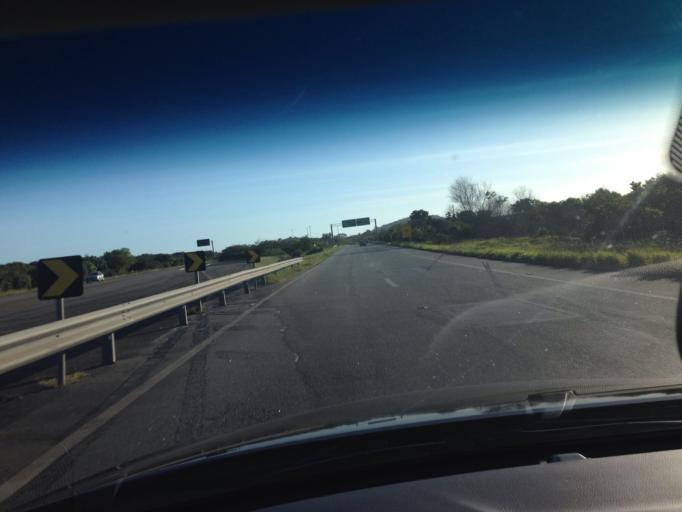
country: BR
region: Espirito Santo
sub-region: Guarapari
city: Guarapari
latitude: -20.6168
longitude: -40.4312
